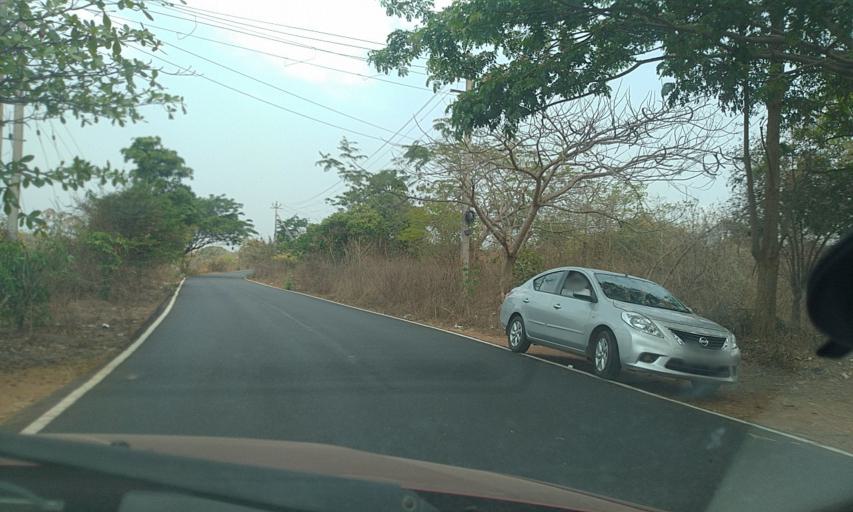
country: IN
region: Goa
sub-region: North Goa
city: Mapuca
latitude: 15.6065
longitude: 73.8021
